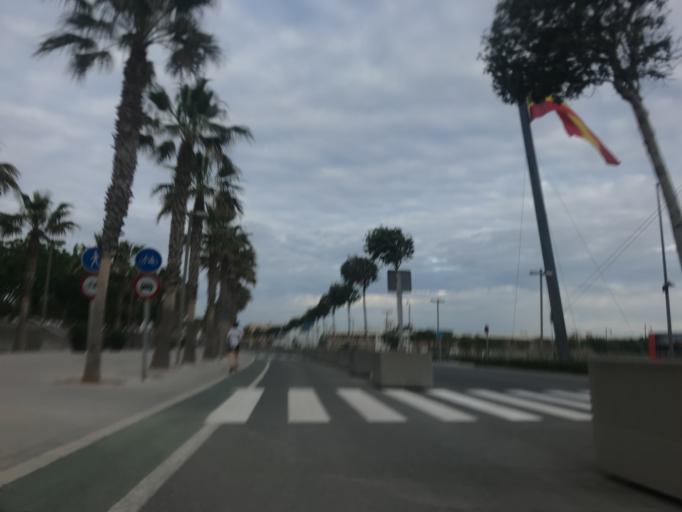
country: ES
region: Valencia
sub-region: Provincia de Valencia
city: Alboraya
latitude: 39.4627
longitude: -0.3220
